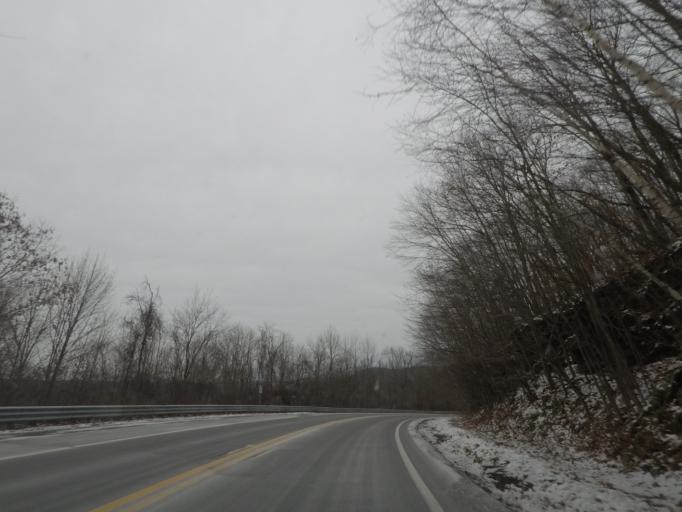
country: US
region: Massachusetts
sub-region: Berkshire County
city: Williamstown
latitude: 42.7083
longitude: -73.2492
